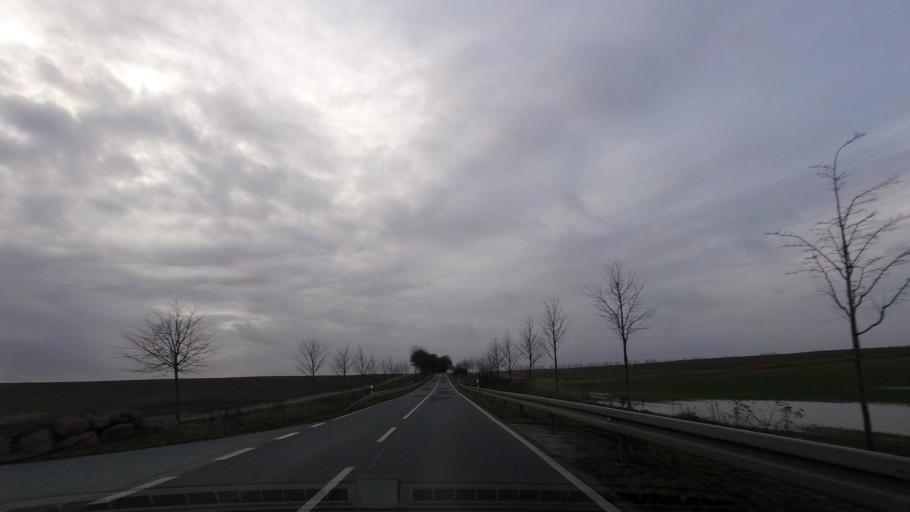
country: DE
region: Mecklenburg-Vorpommern
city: Robel
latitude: 53.3659
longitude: 12.5499
